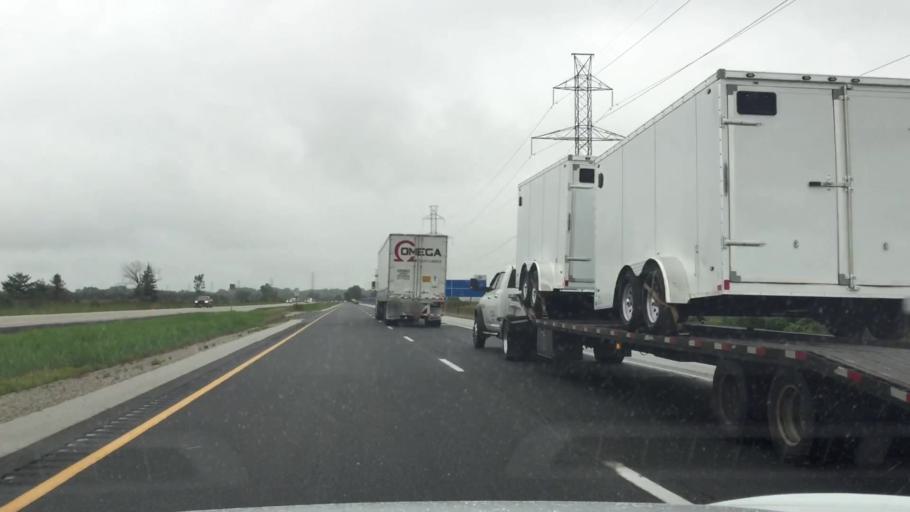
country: CA
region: Ontario
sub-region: Lambton County
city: Walpole Island
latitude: 42.3330
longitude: -82.2168
